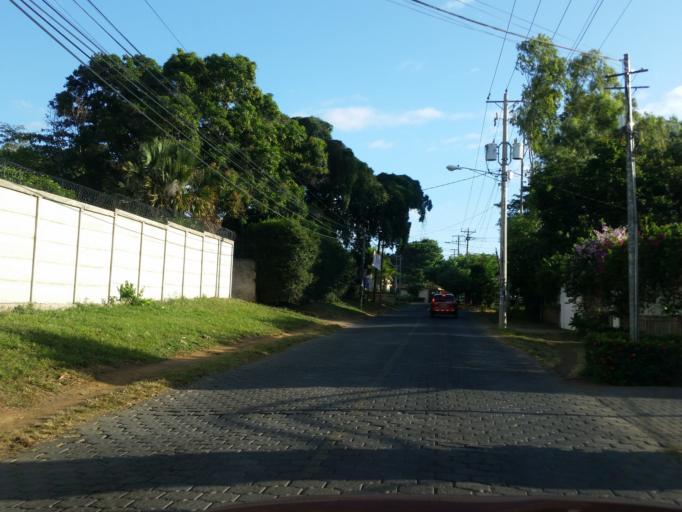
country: NI
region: Managua
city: Managua
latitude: 12.0933
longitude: -86.2344
